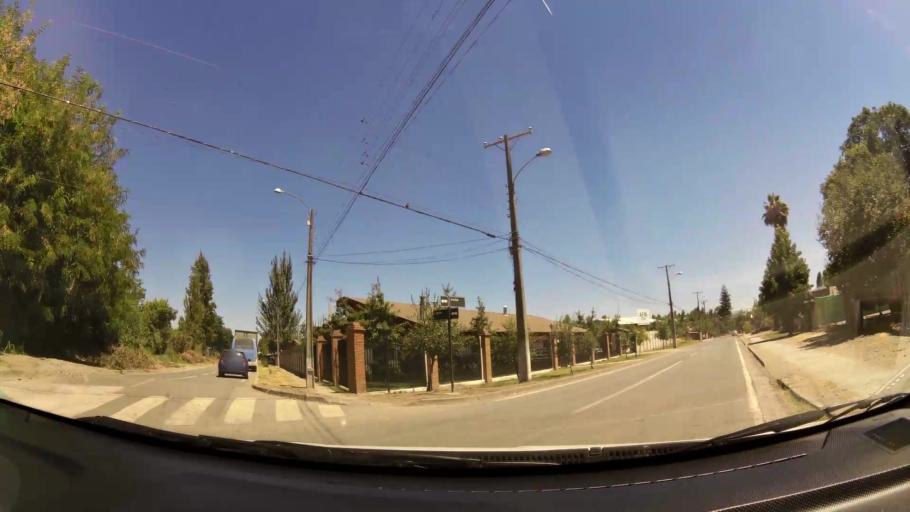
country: CL
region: O'Higgins
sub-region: Provincia de Cachapoal
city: Rancagua
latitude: -34.2277
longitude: -70.7863
